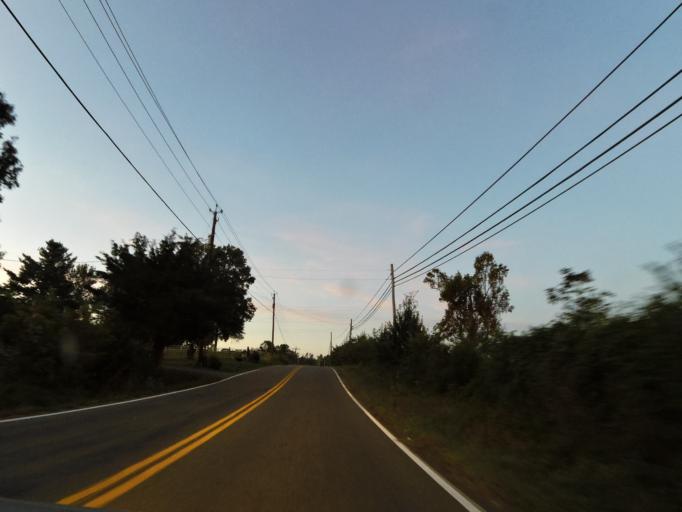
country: US
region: Tennessee
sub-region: Knox County
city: Mascot
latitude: 36.0109
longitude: -83.6414
